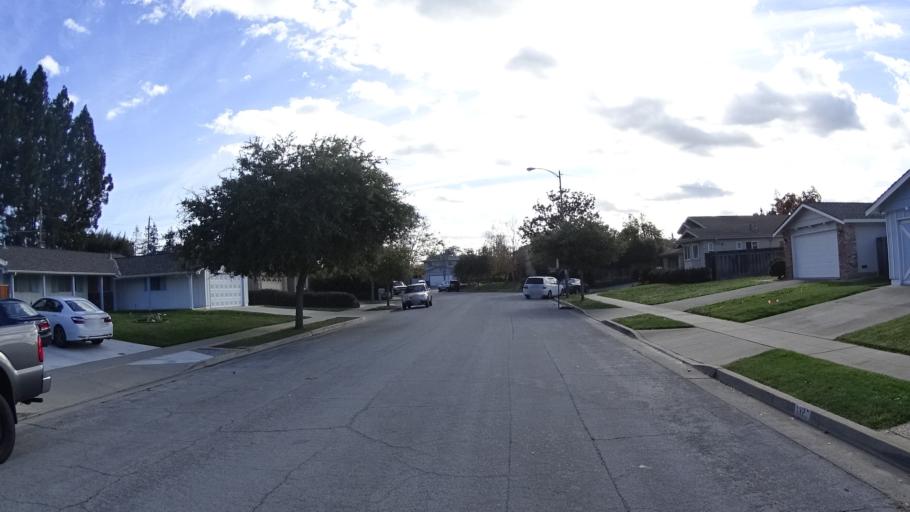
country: US
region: California
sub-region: Santa Clara County
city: Sunnyvale
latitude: 37.3509
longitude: -122.0442
